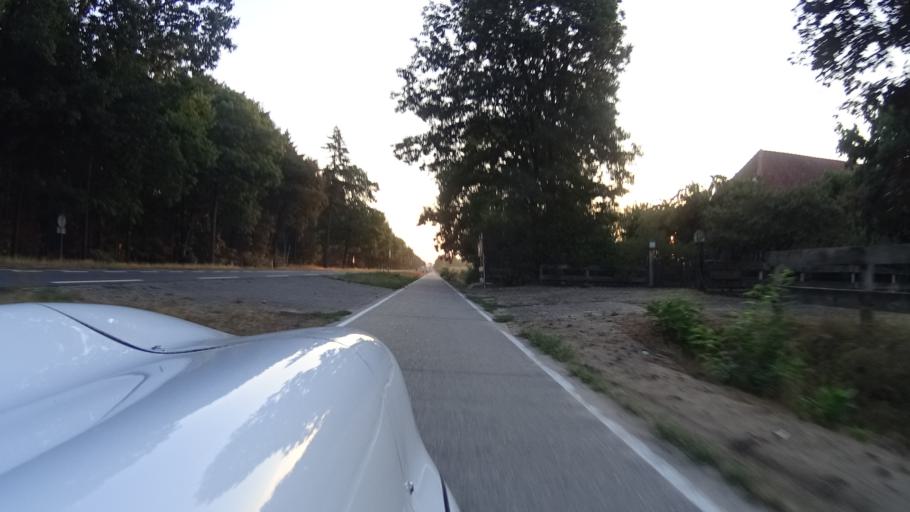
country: NL
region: North Brabant
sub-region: Gemeente Sint Anthonis
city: Sint Anthonis
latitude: 51.5965
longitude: 5.8255
